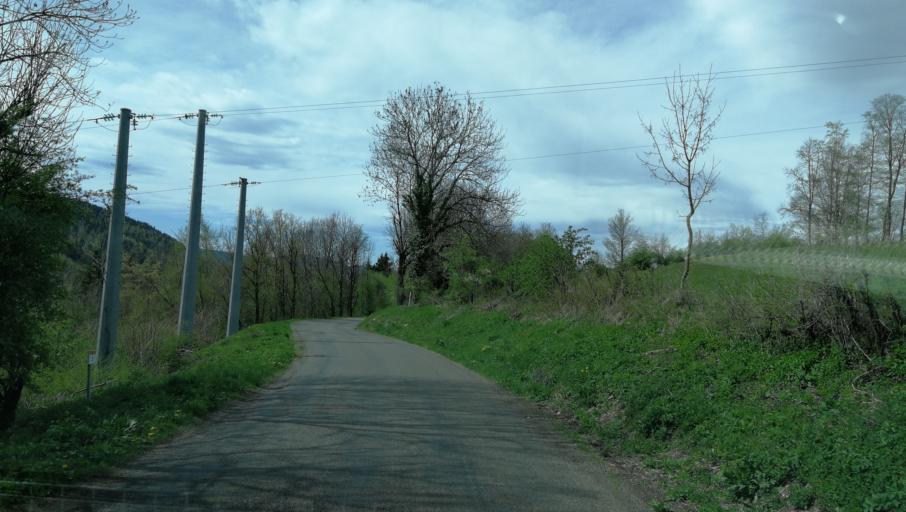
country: FR
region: Rhone-Alpes
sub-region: Departement de l'Ain
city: Arbent
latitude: 46.2433
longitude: 5.7692
